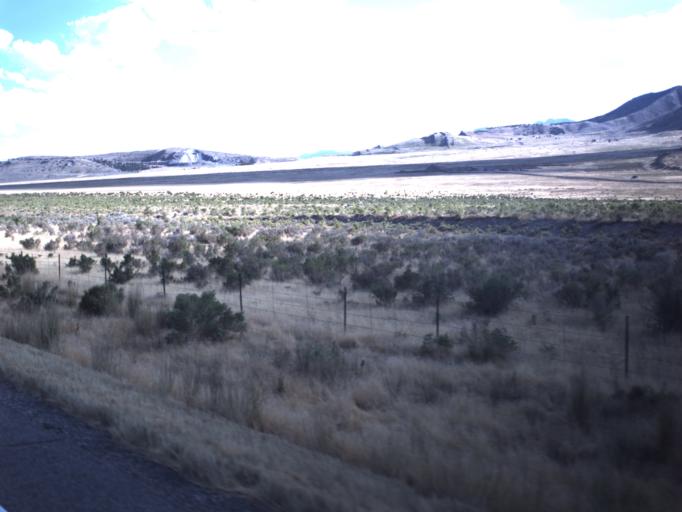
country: US
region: Utah
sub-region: Tooele County
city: Grantsville
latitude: 40.6682
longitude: -112.5450
